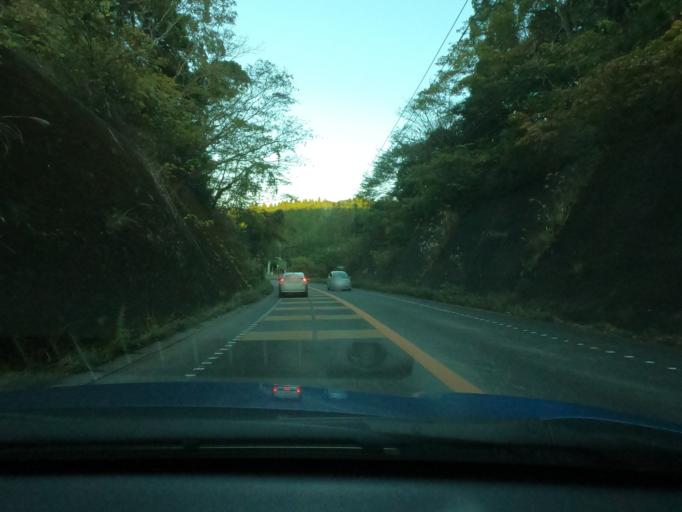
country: JP
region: Kagoshima
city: Satsumasendai
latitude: 31.7960
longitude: 130.4231
